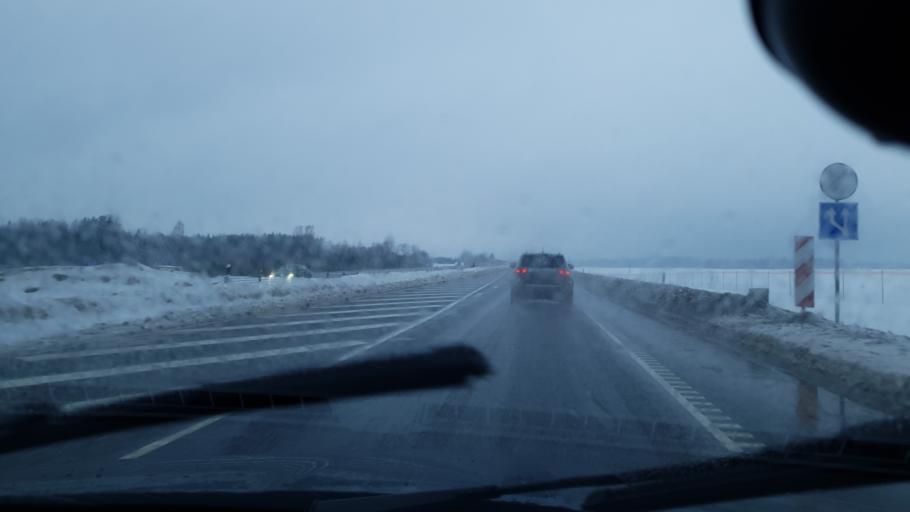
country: EE
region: Harju
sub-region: Raasiku vald
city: Raasiku
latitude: 59.1723
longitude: 25.1544
